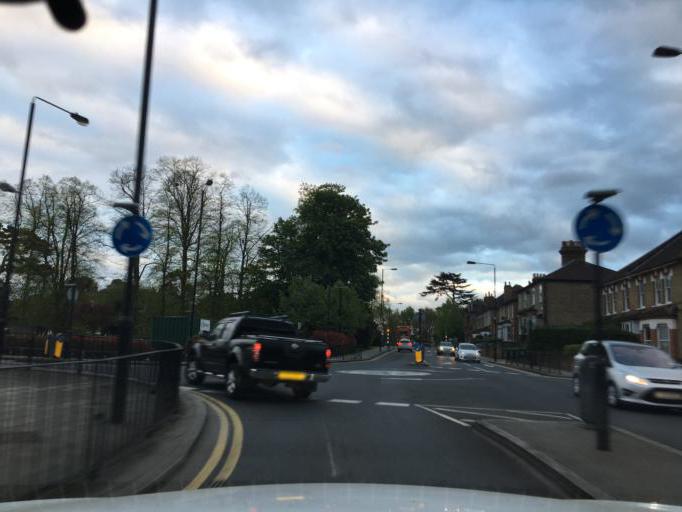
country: GB
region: England
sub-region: Greater London
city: Sidcup
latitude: 51.4252
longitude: 0.1010
